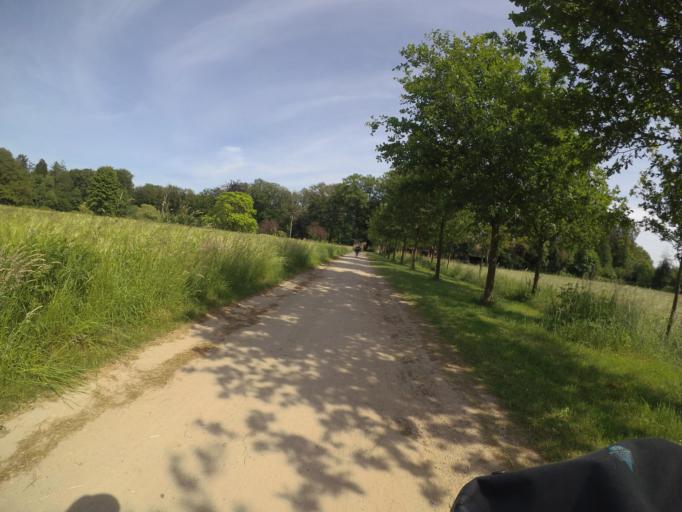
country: NL
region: Gelderland
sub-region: Gemeente Winterswijk
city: Winterswijk
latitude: 51.9362
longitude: 6.6778
